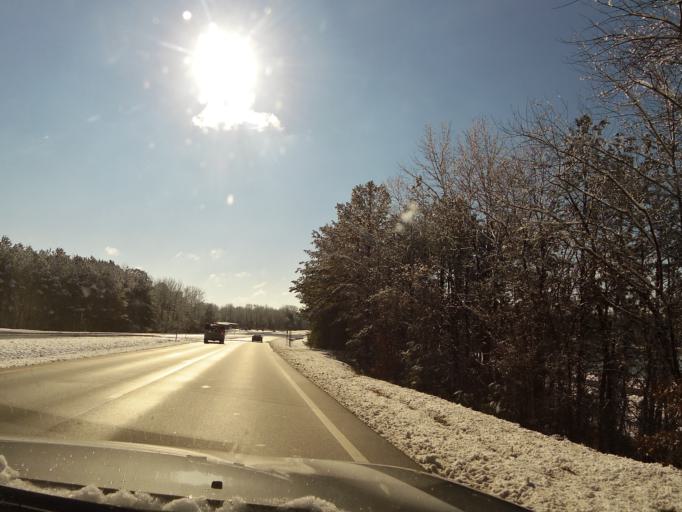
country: US
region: North Carolina
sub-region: Wilson County
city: Elm City
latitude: 35.8187
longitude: -77.8531
